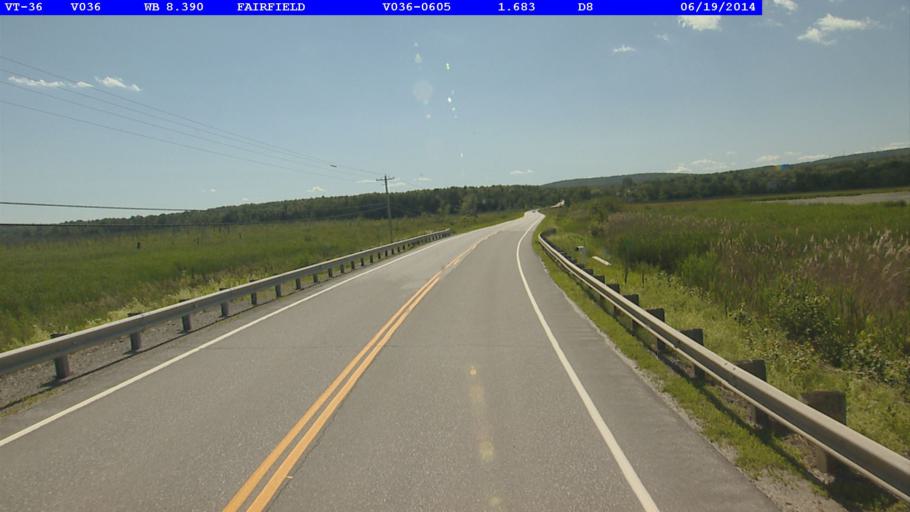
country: US
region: Vermont
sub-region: Franklin County
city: Saint Albans
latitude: 44.7876
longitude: -72.9981
